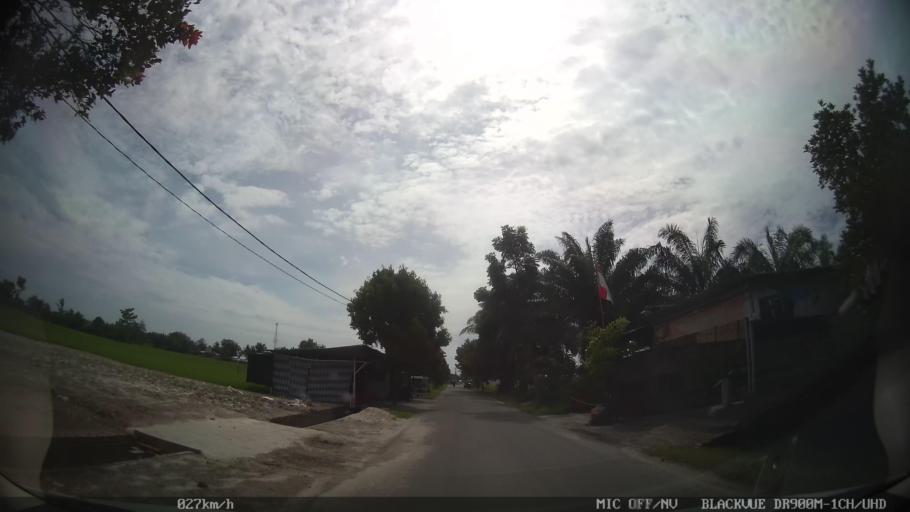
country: ID
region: North Sumatra
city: Percut
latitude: 3.6199
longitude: 98.7924
